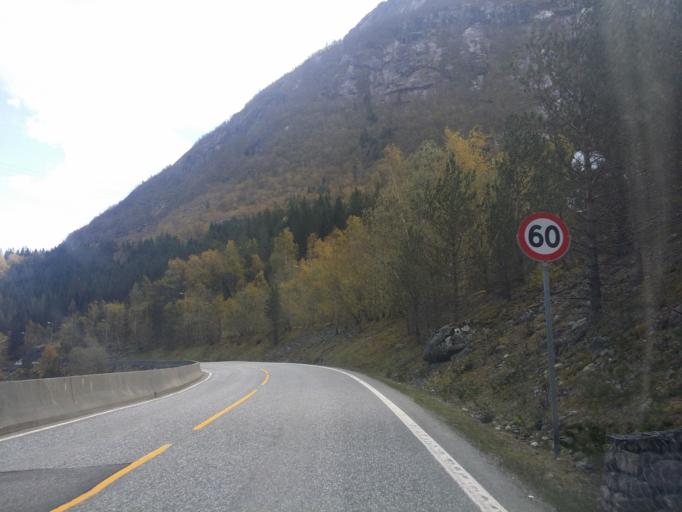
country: NO
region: Hordaland
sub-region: Eidfjord
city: Eidfjord
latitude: 60.4592
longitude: 7.0812
